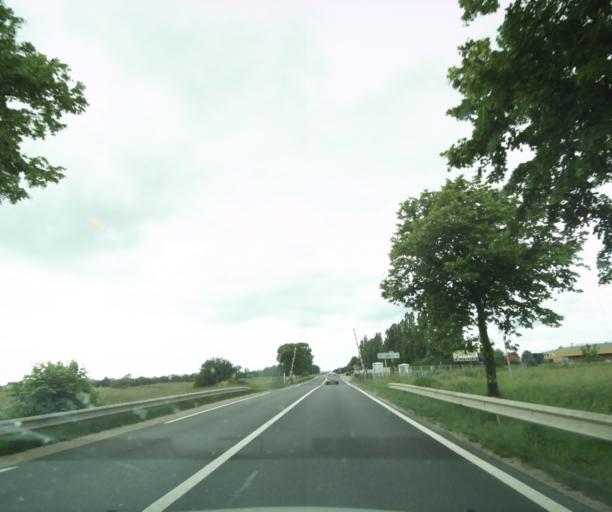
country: FR
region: Centre
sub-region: Departement d'Eure-et-Loir
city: Le Coudray
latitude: 48.4236
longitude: 1.5219
